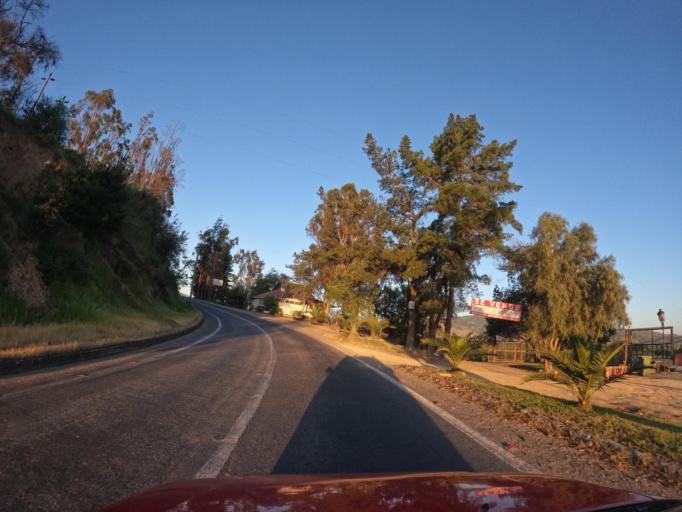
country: CL
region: Maule
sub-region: Provincia de Talca
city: Talca
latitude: -35.0891
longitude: -71.6472
